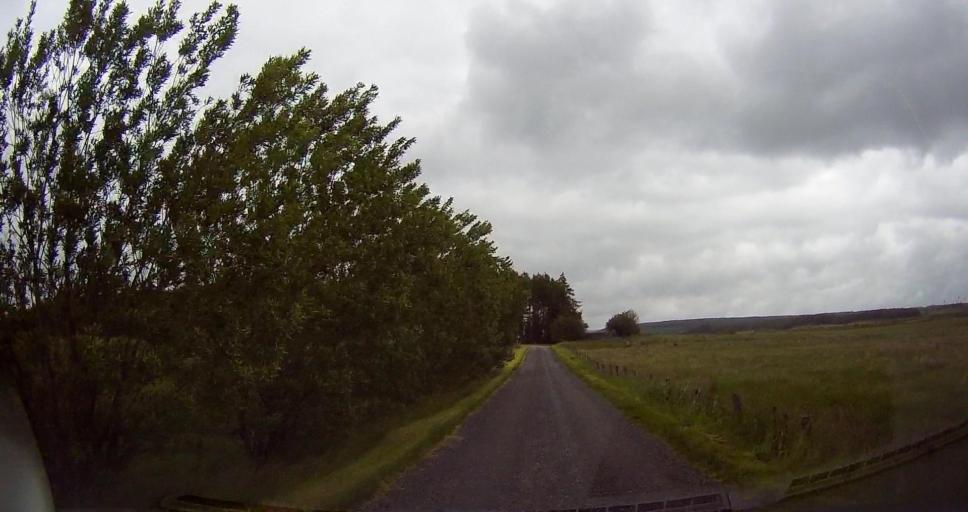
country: GB
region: Scotland
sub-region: Highland
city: Alness
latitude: 58.0657
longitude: -4.4256
